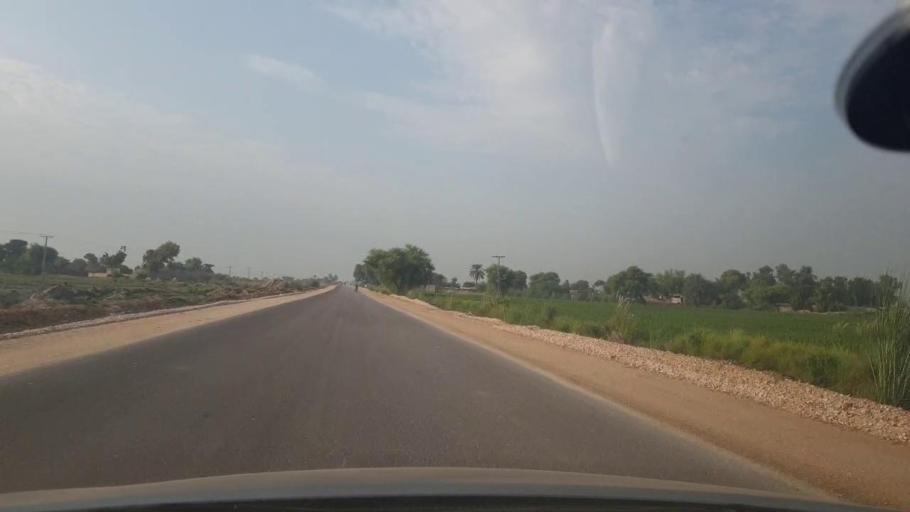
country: PK
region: Sindh
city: Jacobabad
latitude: 28.2014
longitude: 68.3679
